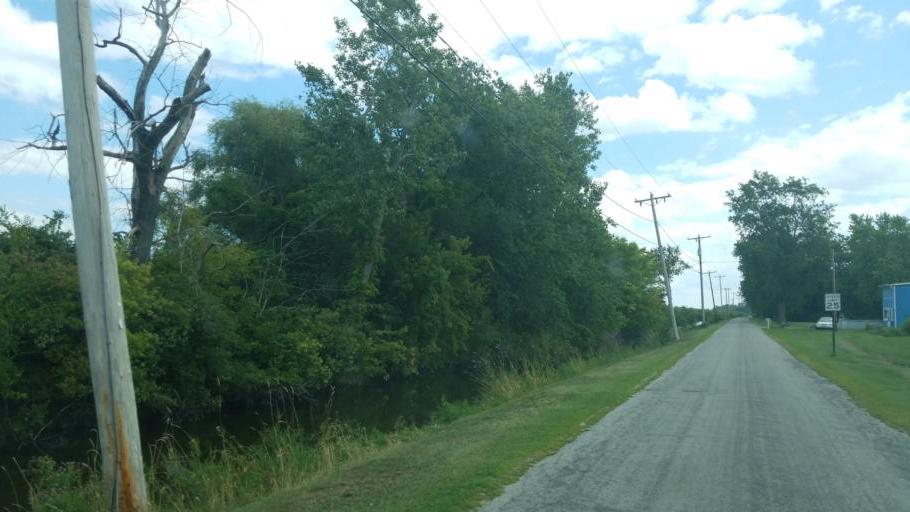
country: US
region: Ohio
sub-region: Lucas County
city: Curtice
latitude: 41.6719
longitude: -83.2787
